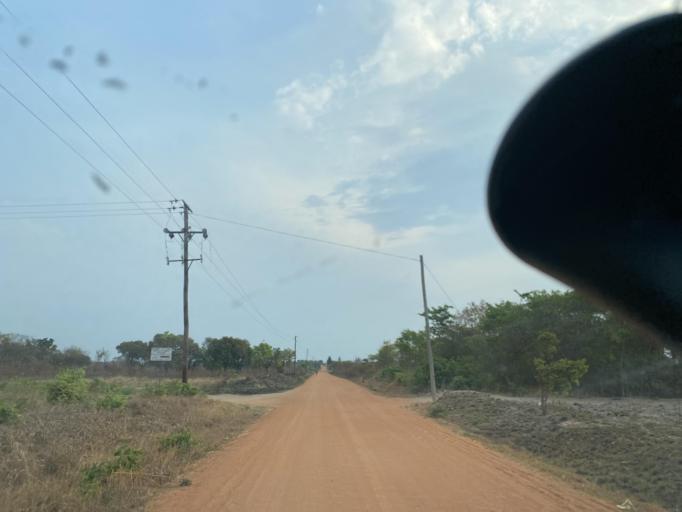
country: ZM
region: Lusaka
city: Chongwe
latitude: -15.2102
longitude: 28.5803
